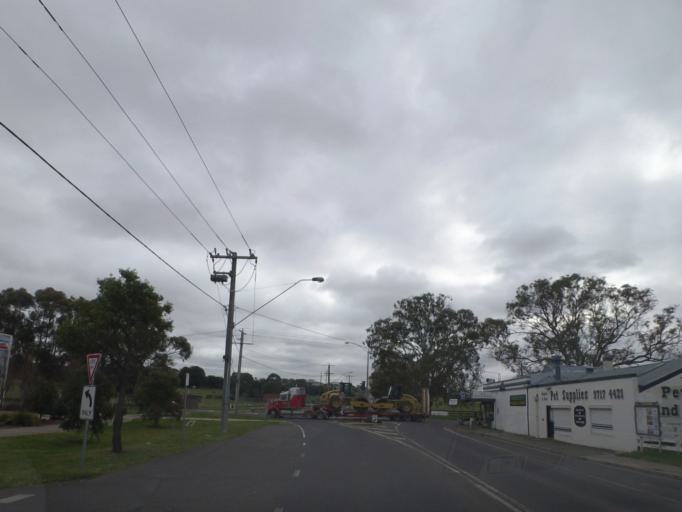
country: AU
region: Victoria
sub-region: Nillumbik
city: Doreen
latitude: -37.6060
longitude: 145.1380
